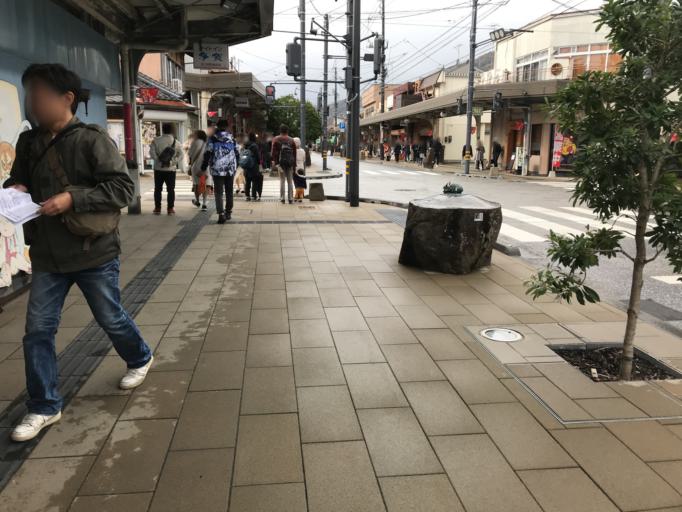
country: JP
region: Shimane
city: Sakaiminato
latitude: 35.5461
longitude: 133.2292
